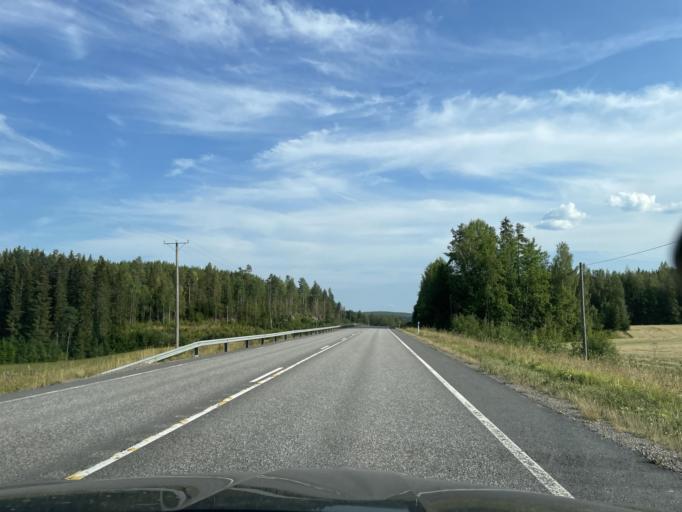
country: FI
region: Central Finland
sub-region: Jaemsae
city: Jaemsae
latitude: 61.7535
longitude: 25.2575
